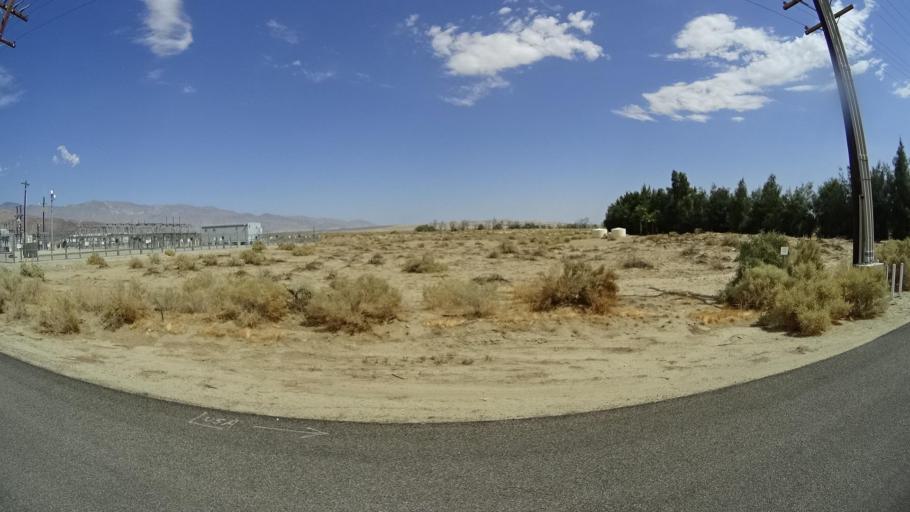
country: US
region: California
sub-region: San Diego County
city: Borrego Springs
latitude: 33.2701
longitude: -116.3485
